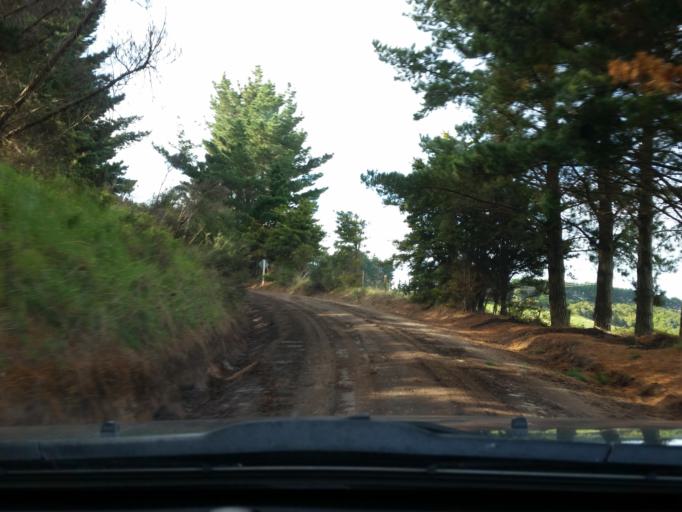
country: NZ
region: Northland
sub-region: Kaipara District
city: Dargaville
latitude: -35.7604
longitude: 173.6101
